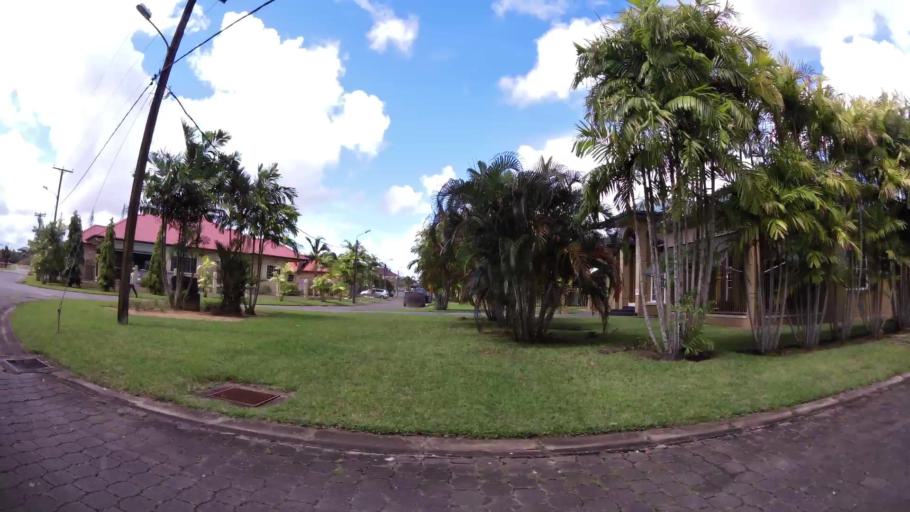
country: SR
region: Paramaribo
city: Paramaribo
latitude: 5.8378
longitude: -55.1933
